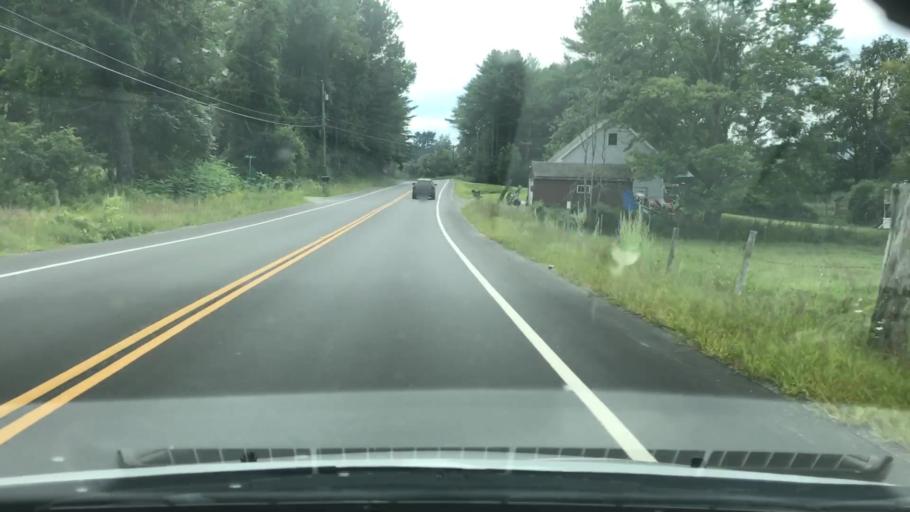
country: US
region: New Hampshire
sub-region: Grafton County
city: Orford
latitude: 43.8918
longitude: -72.1493
